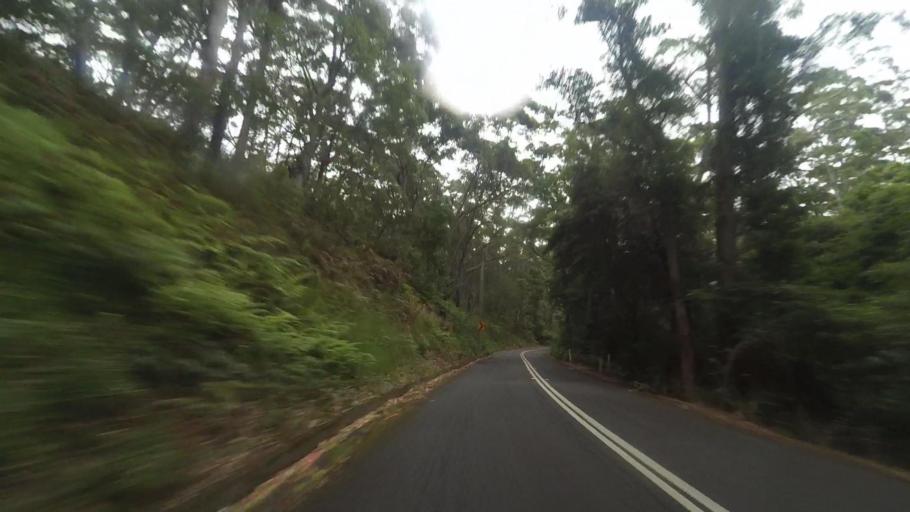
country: AU
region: New South Wales
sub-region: Wollongong
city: Cordeaux Heights
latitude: -34.4330
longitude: 150.8084
